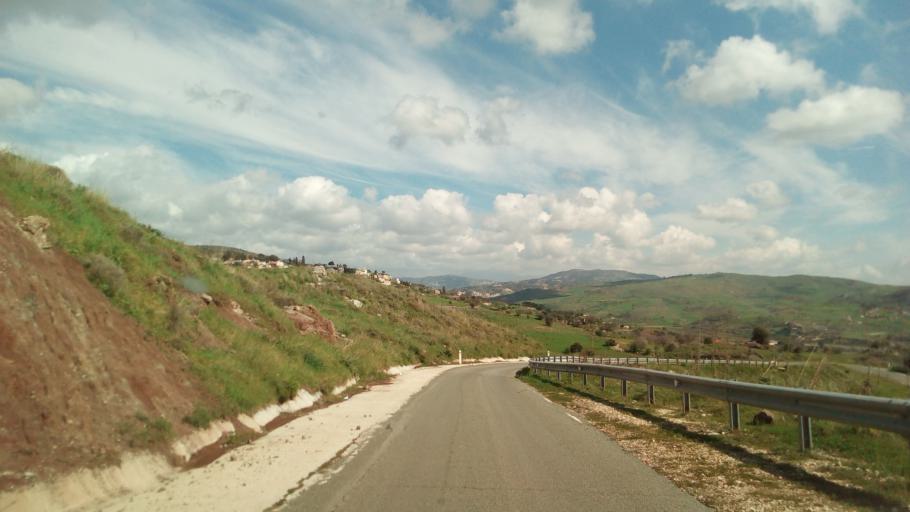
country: CY
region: Pafos
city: Mesogi
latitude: 34.7722
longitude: 32.5637
